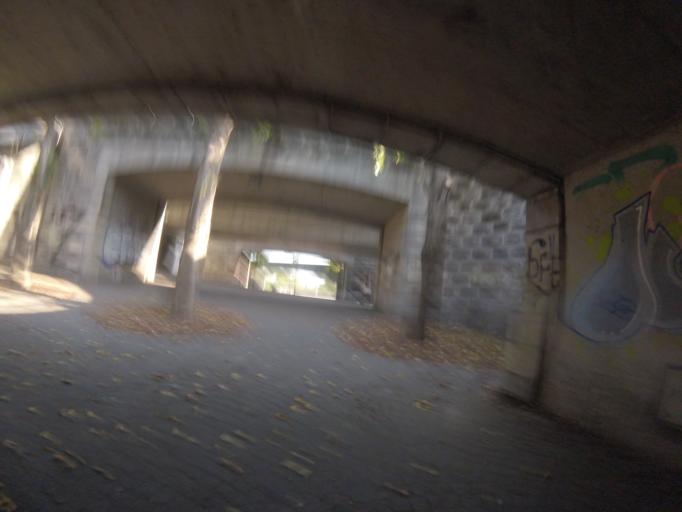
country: NE
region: Dosso
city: Dosso
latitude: 12.6987
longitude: 3.0498
